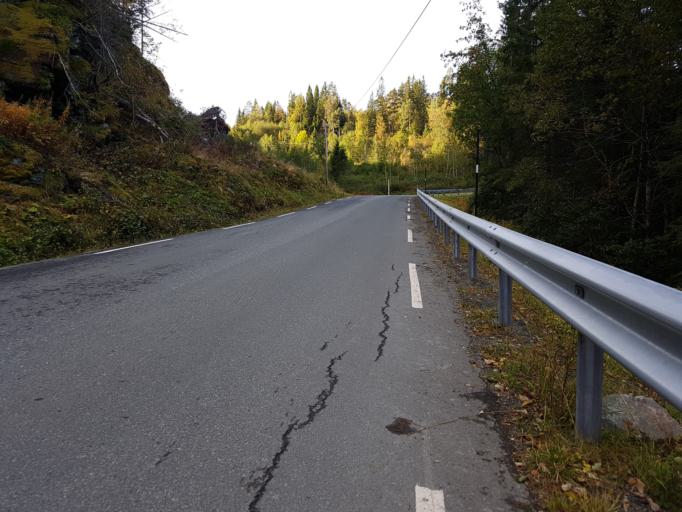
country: NO
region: Sor-Trondelag
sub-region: Klaebu
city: Klaebu
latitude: 63.3459
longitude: 10.5383
